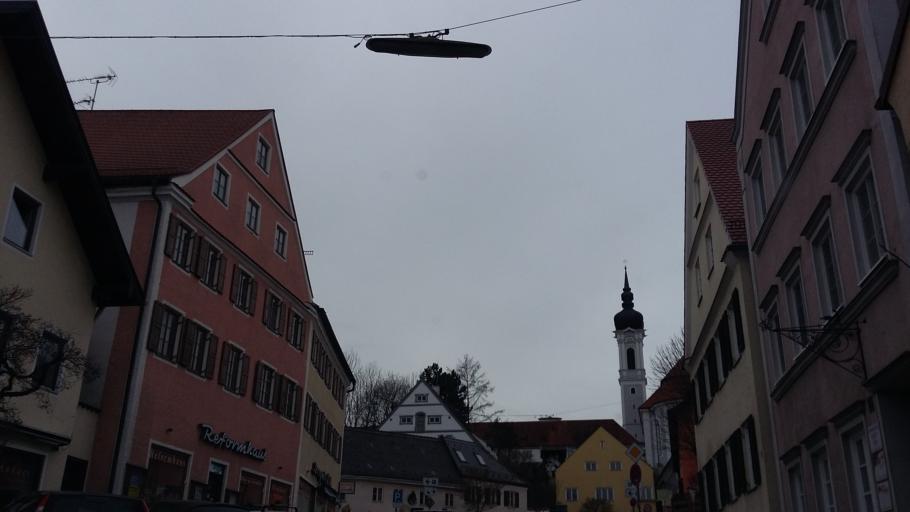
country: DE
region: Bavaria
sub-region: Upper Bavaria
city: Diessen am Ammersee
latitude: 47.9482
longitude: 11.1005
